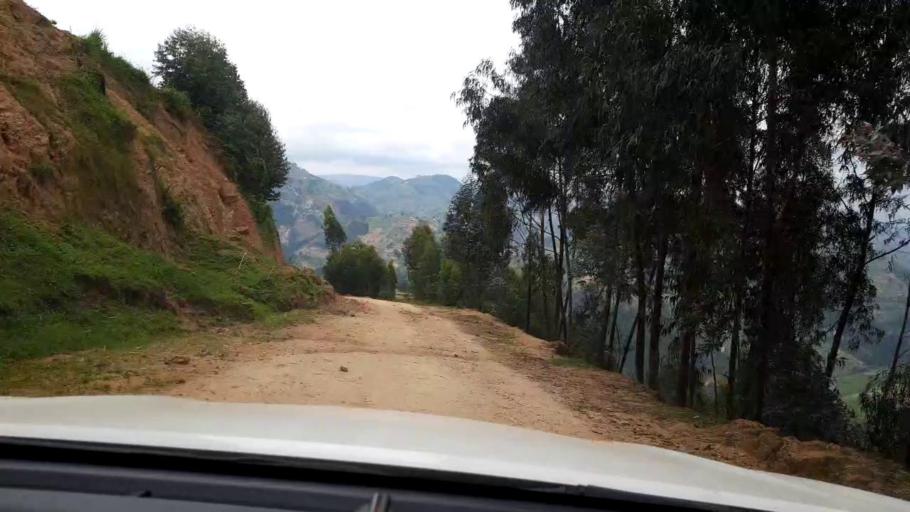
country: RW
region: Western Province
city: Kibuye
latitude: -1.8273
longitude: 29.5471
